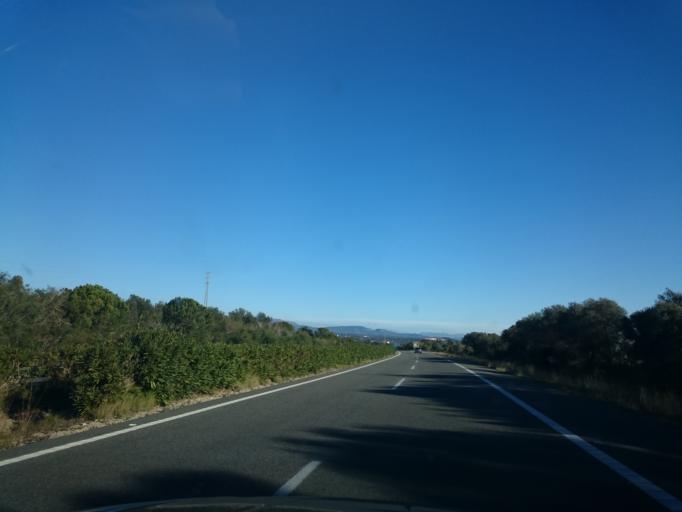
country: ES
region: Catalonia
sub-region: Provincia de Tarragona
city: Masdenverge
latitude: 40.7076
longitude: 0.5517
